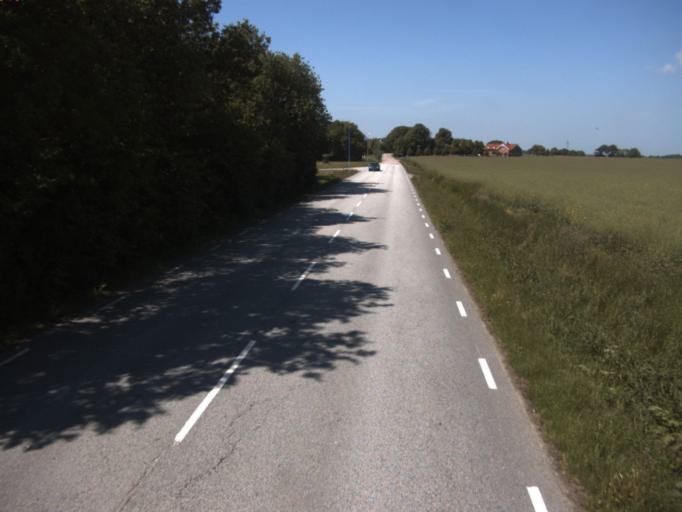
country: SE
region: Skane
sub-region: Helsingborg
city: Barslov
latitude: 56.0075
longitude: 12.8138
